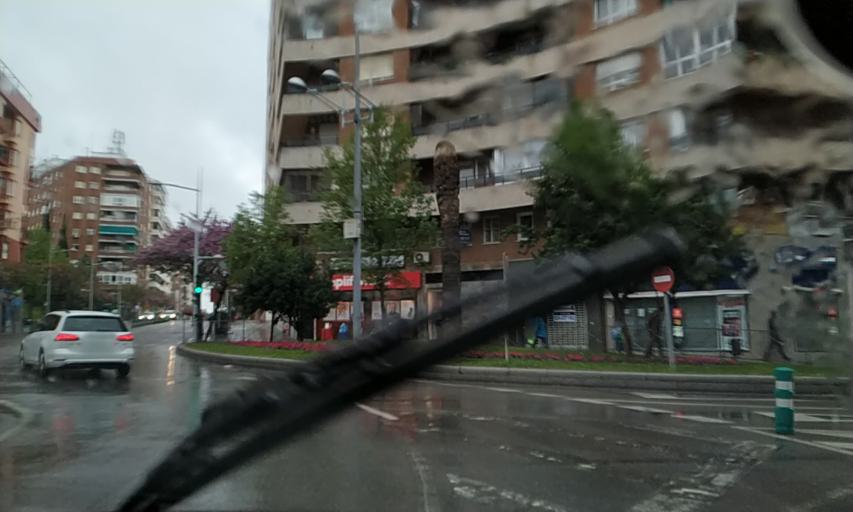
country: ES
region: Extremadura
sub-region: Provincia de Badajoz
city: Badajoz
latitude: 38.8732
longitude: -6.9729
